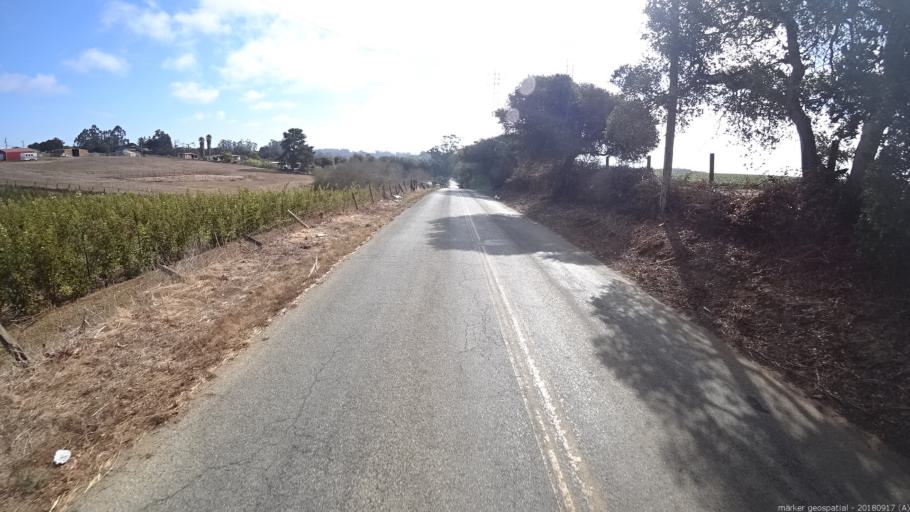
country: US
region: California
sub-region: Monterey County
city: Prunedale
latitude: 36.7891
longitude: -121.7043
